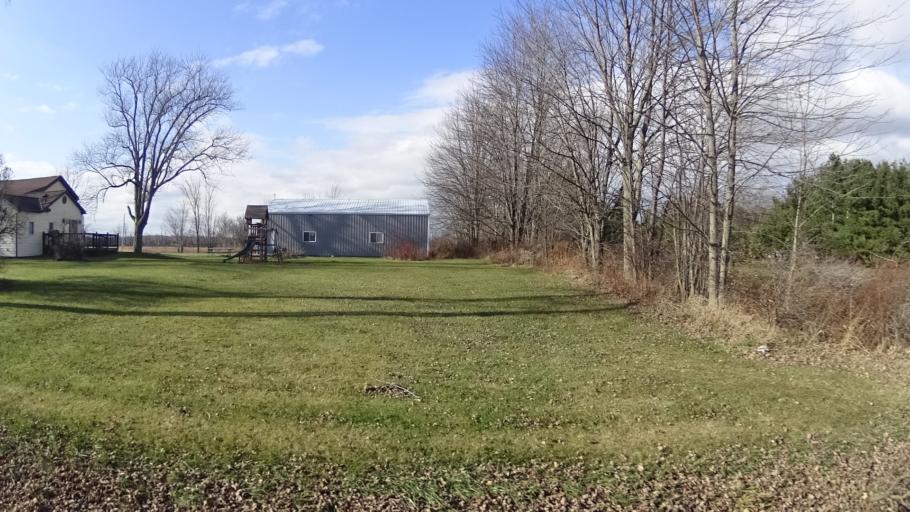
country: US
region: Ohio
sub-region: Lorain County
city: Camden
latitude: 41.2383
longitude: -82.2894
